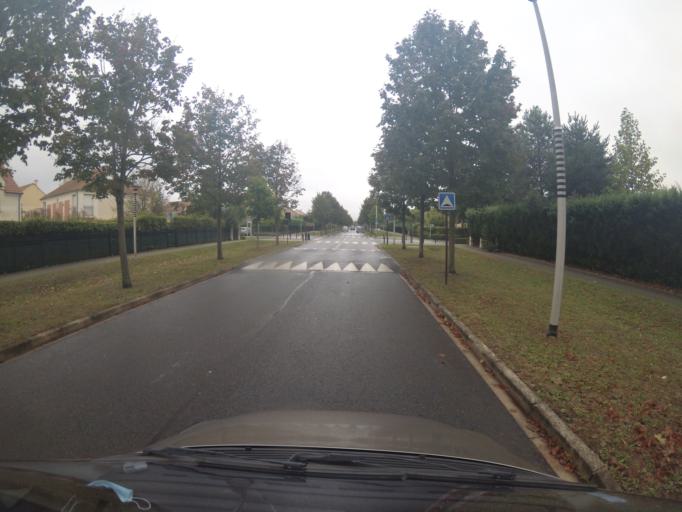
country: FR
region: Ile-de-France
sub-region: Departement de Seine-et-Marne
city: Chanteloup-en-Brie
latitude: 48.8431
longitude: 2.7319
